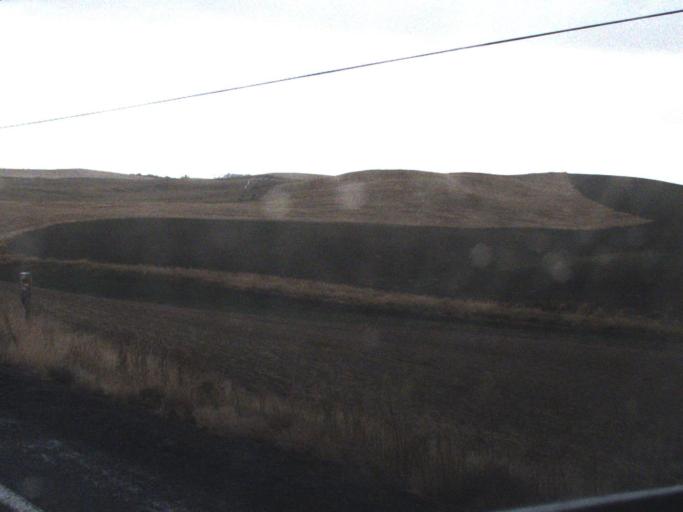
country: US
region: Washington
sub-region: Lincoln County
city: Davenport
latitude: 47.6788
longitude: -118.1410
